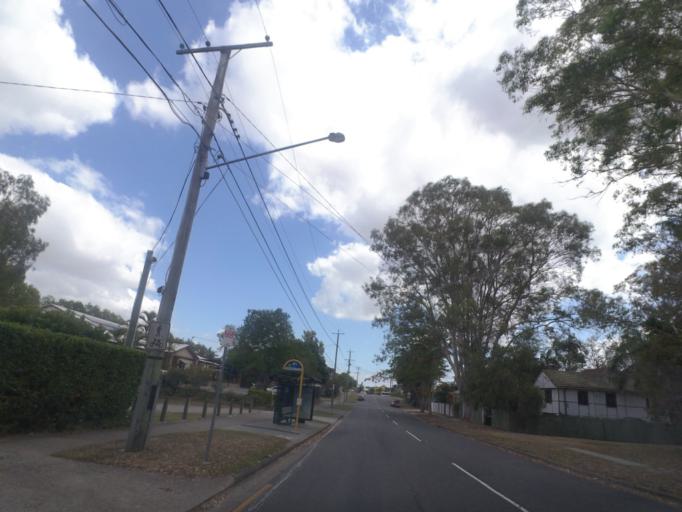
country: AU
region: Queensland
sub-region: Brisbane
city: Carindale
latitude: -27.4975
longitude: 153.0940
